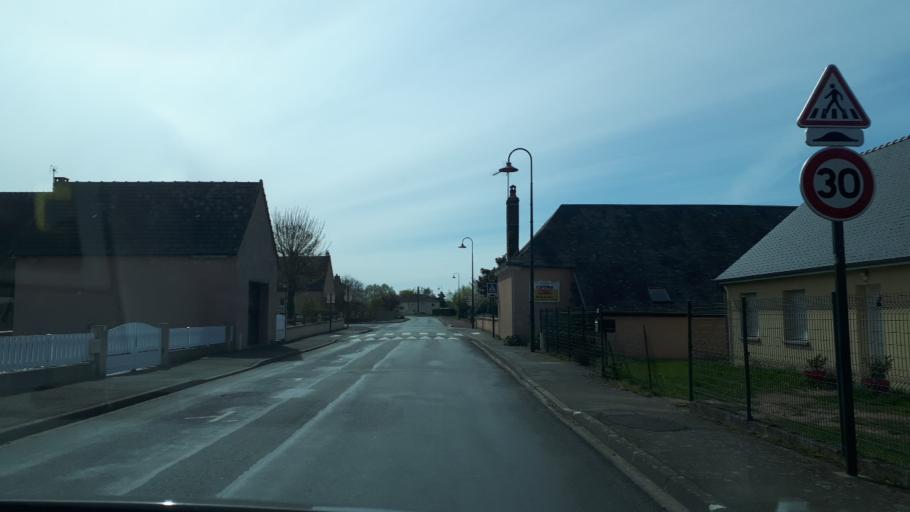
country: FR
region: Pays de la Loire
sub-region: Departement de la Sarthe
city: Saint-Ouen-en-Belin
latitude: 47.8315
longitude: 0.2115
